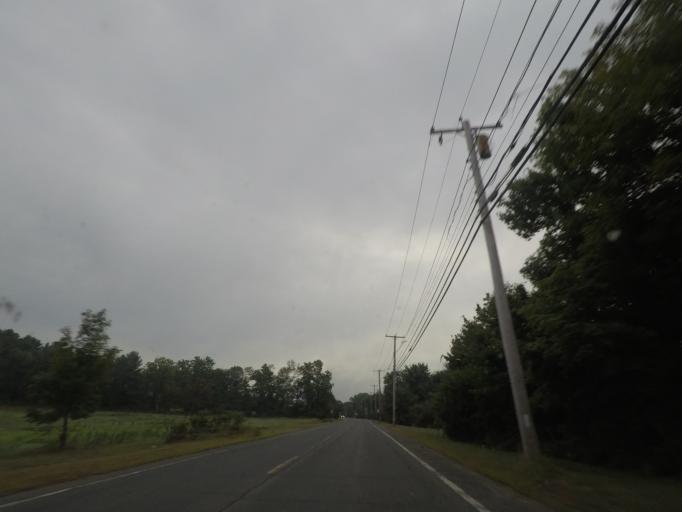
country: US
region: Massachusetts
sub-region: Hampden County
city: Palmer
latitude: 42.1443
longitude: -72.2916
